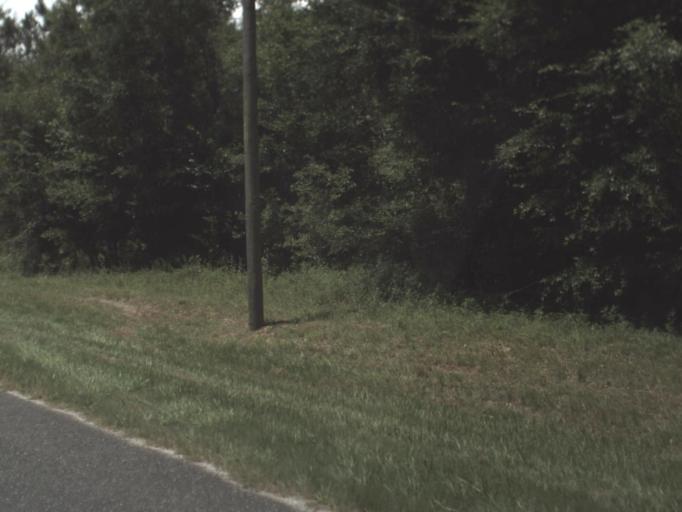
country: US
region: Florida
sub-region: Lafayette County
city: Mayo
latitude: 30.0236
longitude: -82.9388
